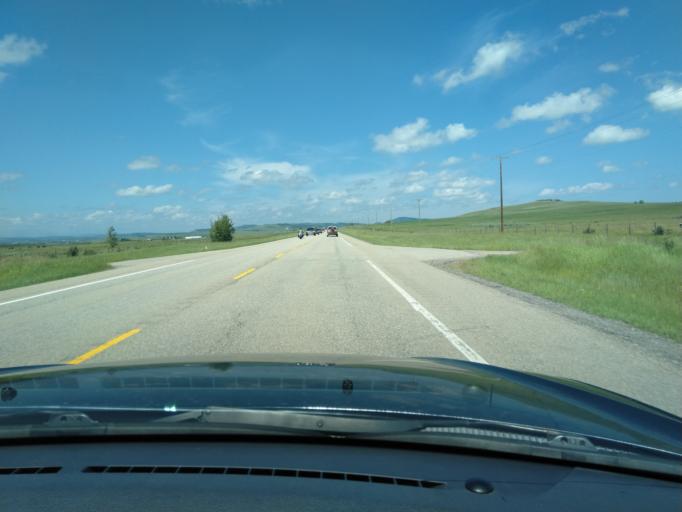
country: CA
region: Alberta
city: Cochrane
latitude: 51.2109
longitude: -114.5255
